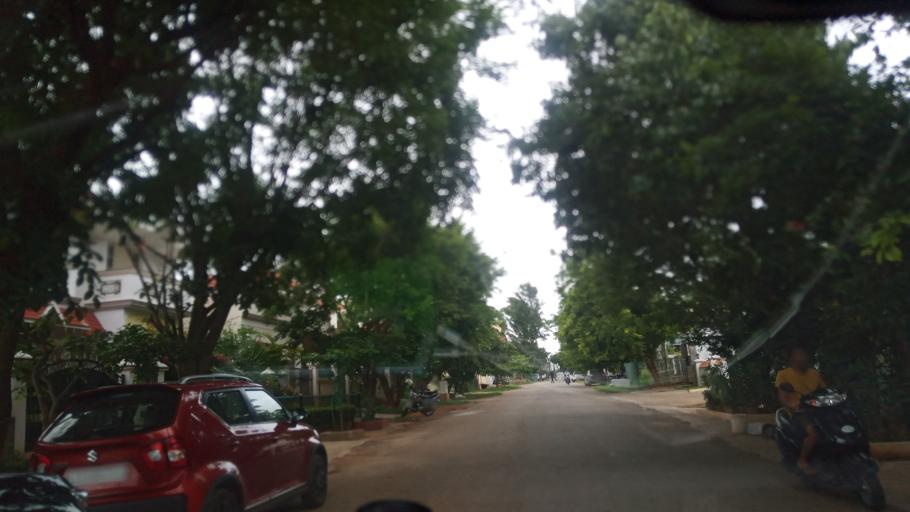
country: IN
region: Karnataka
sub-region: Mysore
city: Mysore
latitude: 12.2885
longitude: 76.6122
